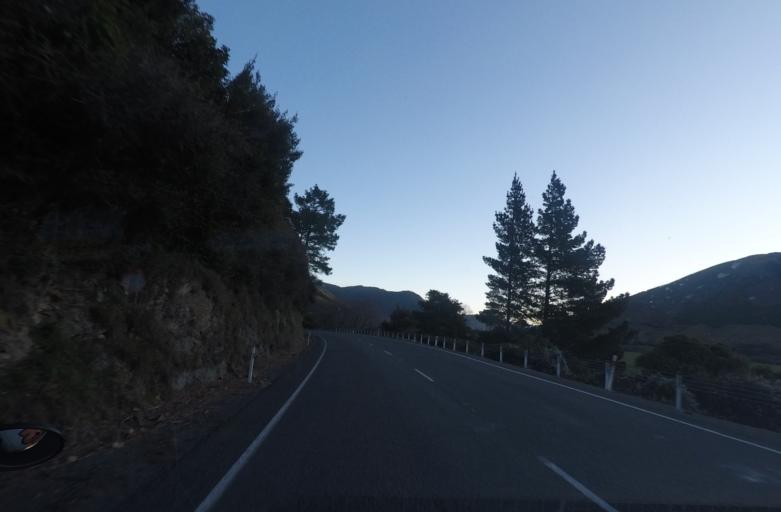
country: NZ
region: Marlborough
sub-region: Marlborough District
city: Picton
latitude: -41.2753
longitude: 173.7322
